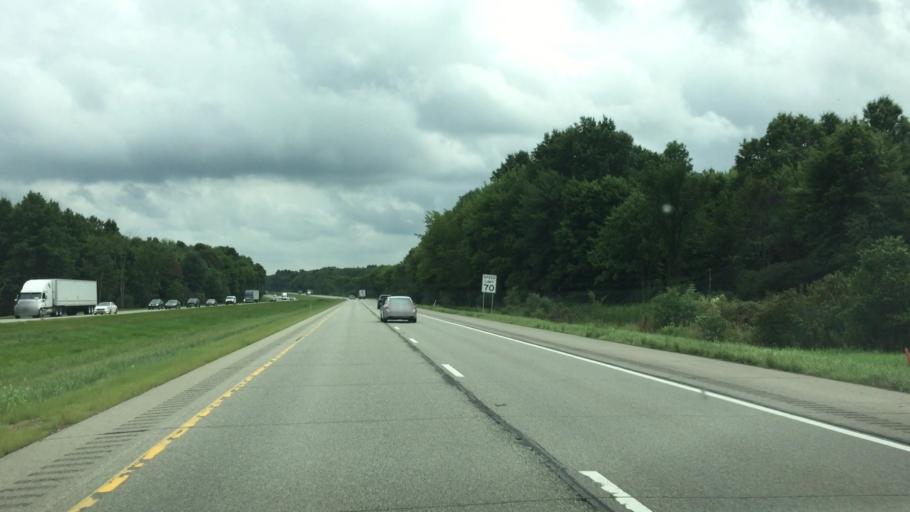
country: US
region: Pennsylvania
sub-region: Mercer County
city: Grove City
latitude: 41.0930
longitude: -80.1400
